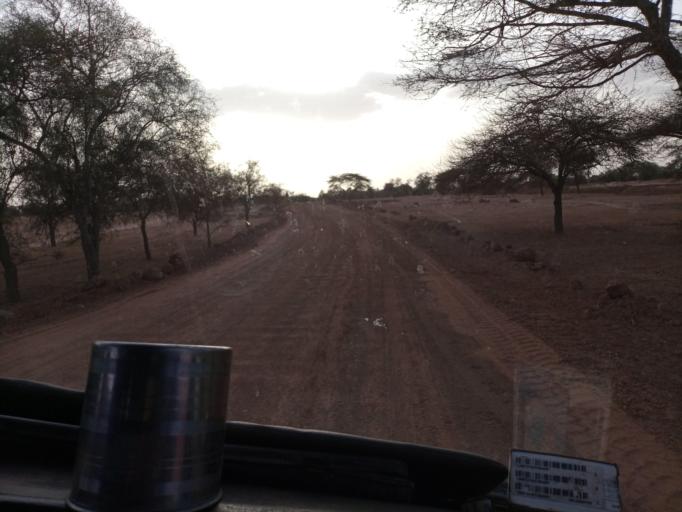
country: SN
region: Louga
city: Dara
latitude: 15.3702
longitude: -15.5783
